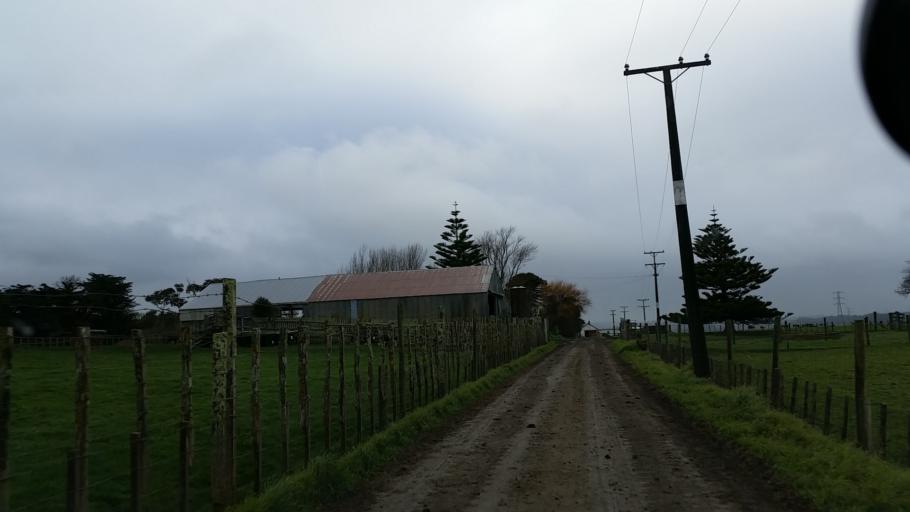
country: NZ
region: Taranaki
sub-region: South Taranaki District
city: Patea
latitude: -39.7691
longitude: 174.7072
